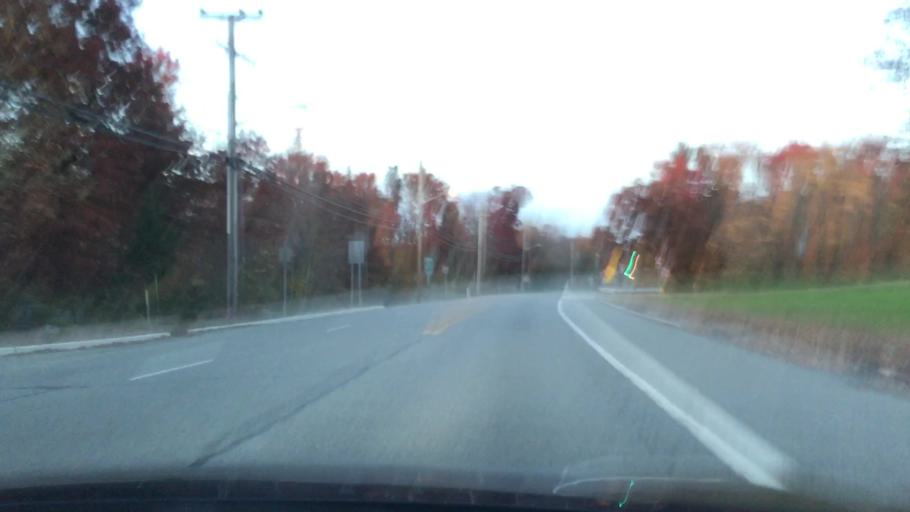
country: US
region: New Jersey
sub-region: Bergen County
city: Alpine
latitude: 40.9542
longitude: -73.9226
